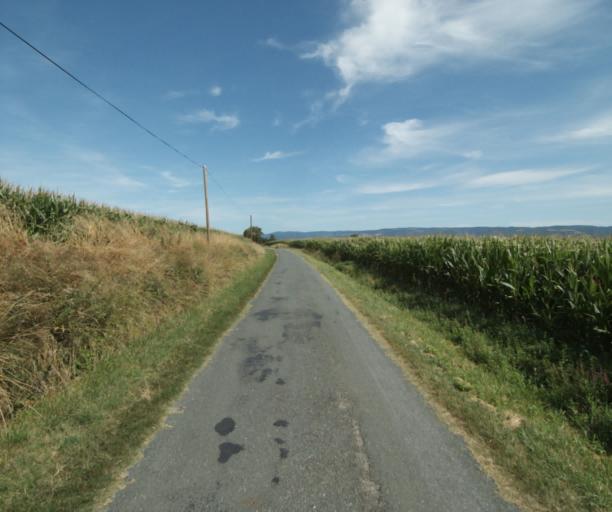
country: FR
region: Midi-Pyrenees
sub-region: Departement du Tarn
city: Puylaurens
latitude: 43.5259
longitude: 2.0140
